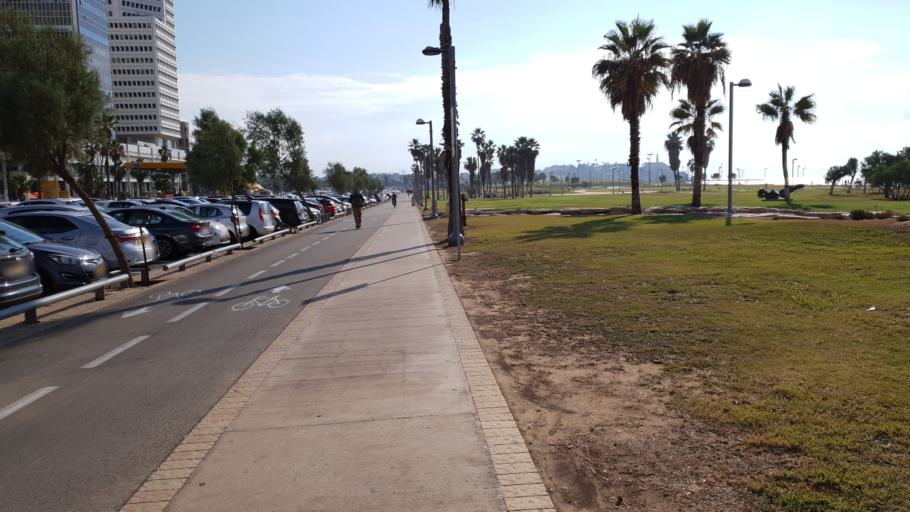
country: IL
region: Tel Aviv
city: Yafo
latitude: 32.0654
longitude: 34.7620
